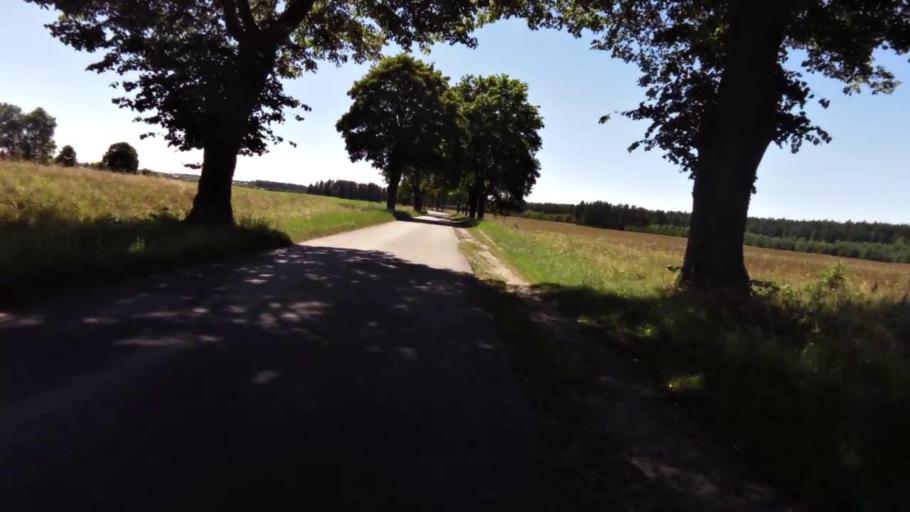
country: PL
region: West Pomeranian Voivodeship
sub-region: Powiat szczecinecki
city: Bialy Bor
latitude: 53.9188
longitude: 16.8405
